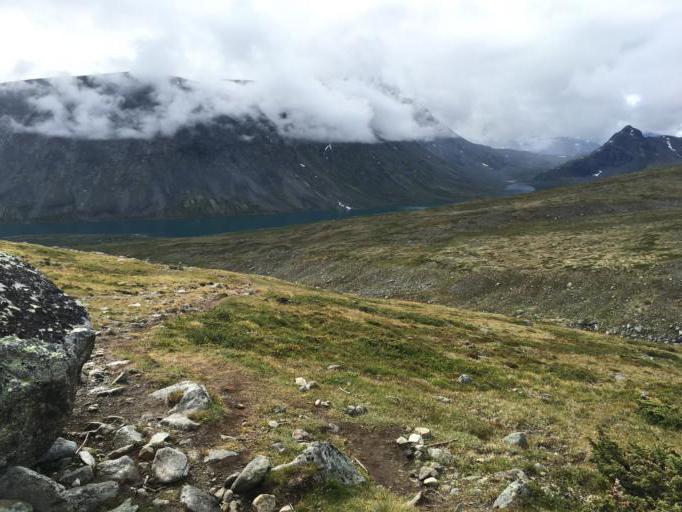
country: NO
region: Oppland
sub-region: Lom
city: Fossbergom
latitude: 61.5721
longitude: 8.6731
